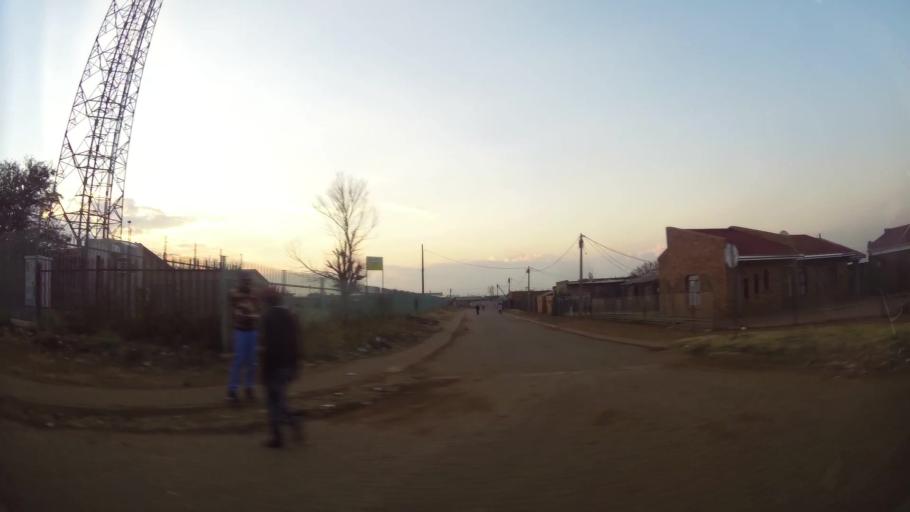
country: ZA
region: Gauteng
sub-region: City of Johannesburg Metropolitan Municipality
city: Orange Farm
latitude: -26.5533
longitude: 27.8705
